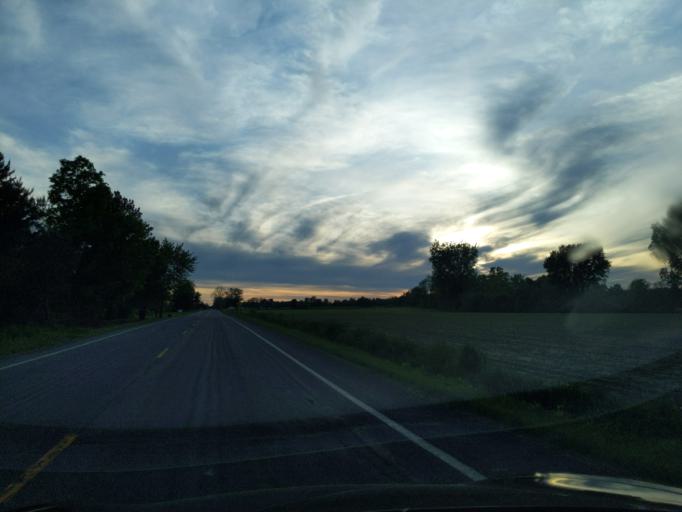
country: US
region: Michigan
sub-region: Ingham County
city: Williamston
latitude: 42.6008
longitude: -84.3347
